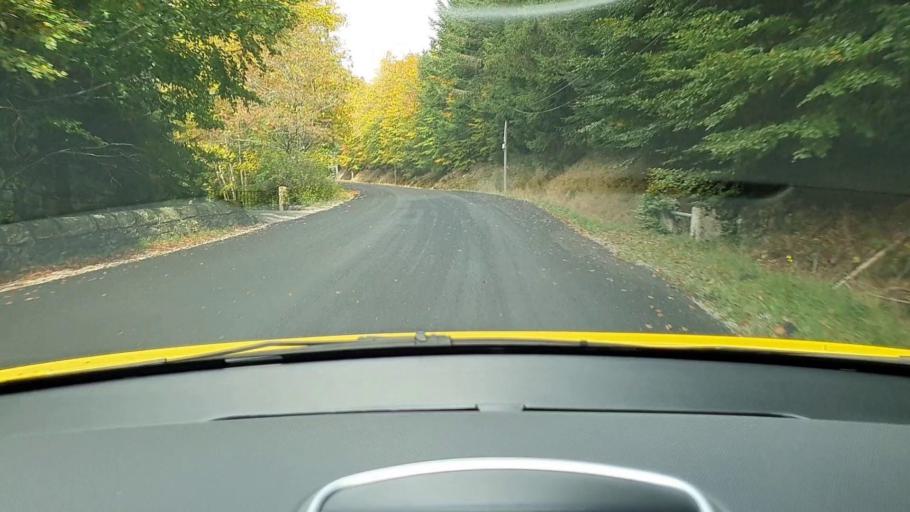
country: FR
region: Languedoc-Roussillon
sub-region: Departement du Gard
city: Valleraugue
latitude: 44.0866
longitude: 3.5392
